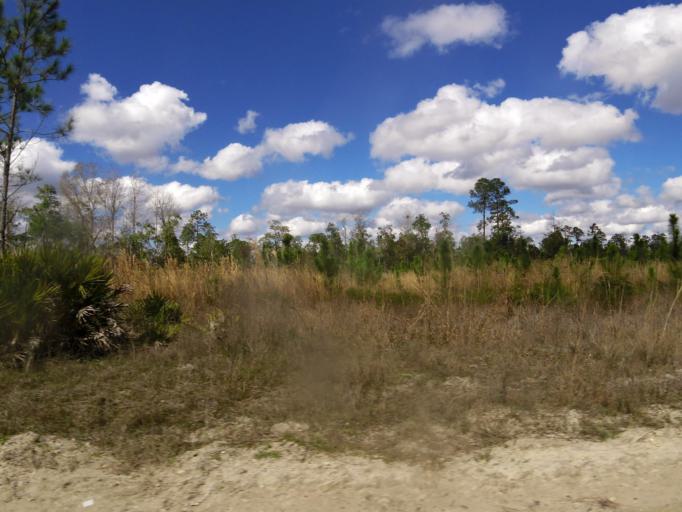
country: US
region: Florida
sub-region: Clay County
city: Green Cove Springs
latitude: 29.8518
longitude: -81.7208
